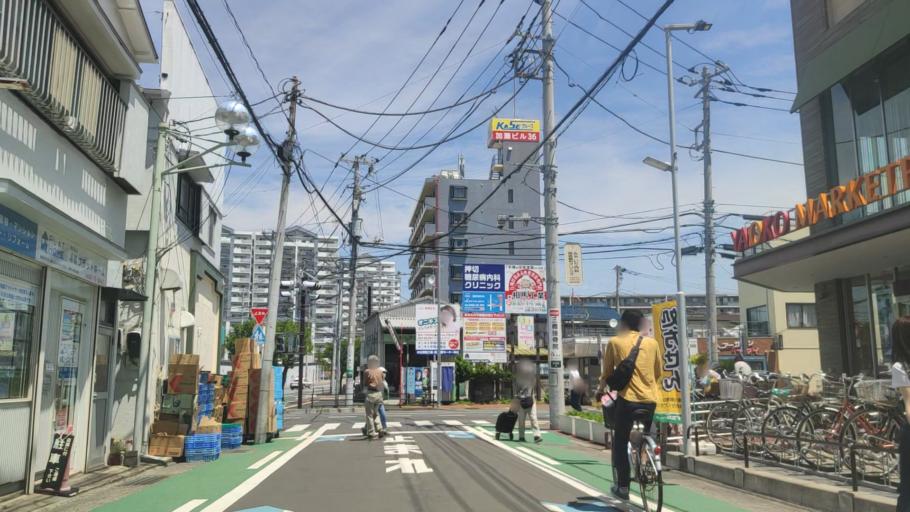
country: JP
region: Kanagawa
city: Hiratsuka
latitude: 35.3347
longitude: 139.3507
